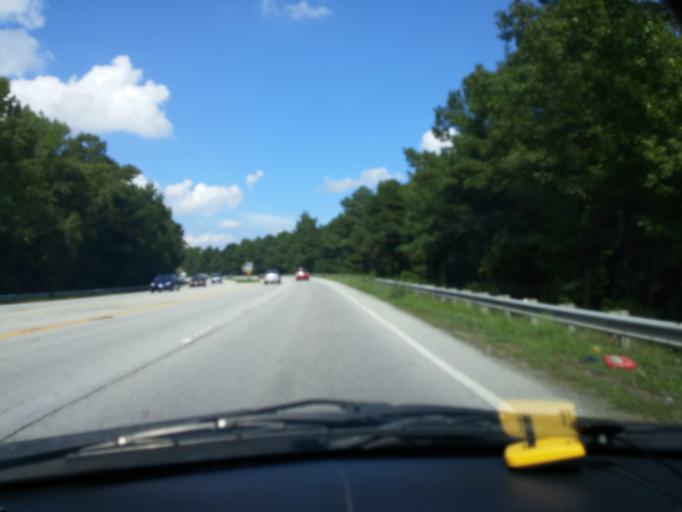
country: US
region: North Carolina
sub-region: Pitt County
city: Greenville
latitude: 35.6088
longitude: -77.3291
